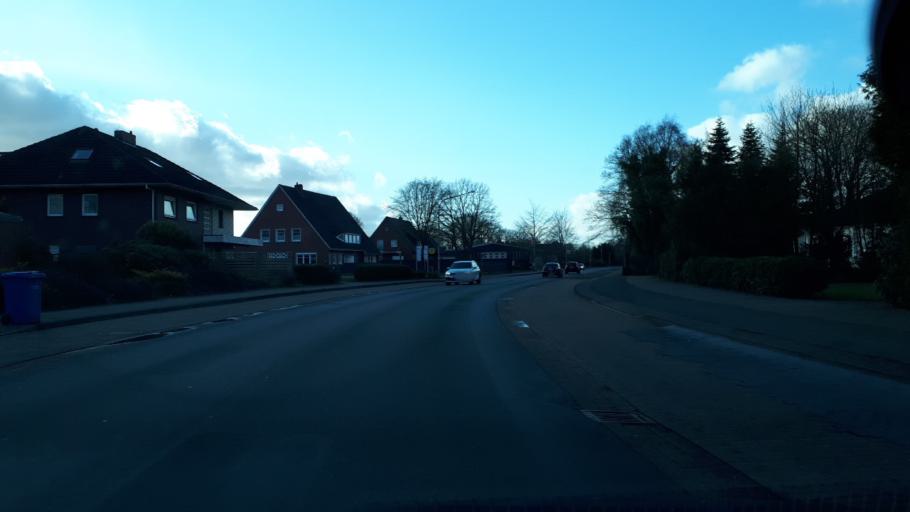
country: DE
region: Lower Saxony
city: Molbergen
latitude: 52.8593
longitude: 7.9156
